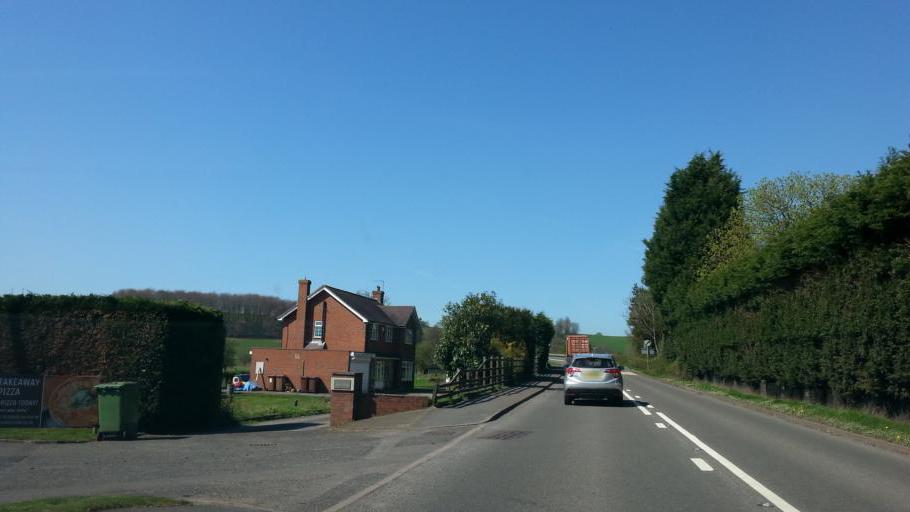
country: GB
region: England
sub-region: Staffordshire
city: Stafford
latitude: 52.8410
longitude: -2.0435
